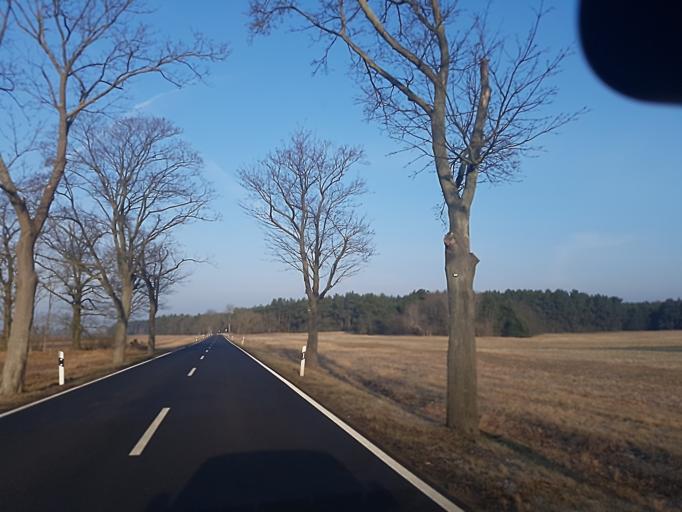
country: DE
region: Brandenburg
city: Golzow
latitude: 52.2679
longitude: 12.6471
